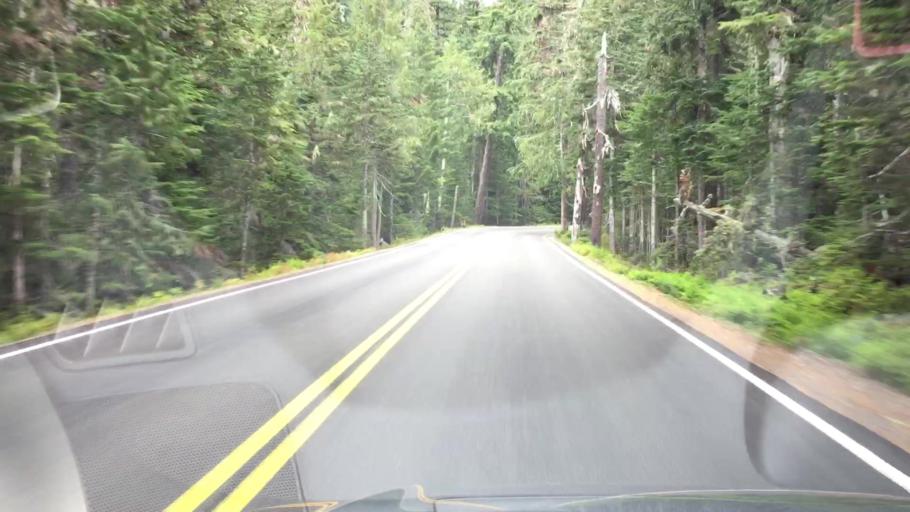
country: US
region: Washington
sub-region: Pierce County
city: Buckley
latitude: 46.7723
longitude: -121.7857
